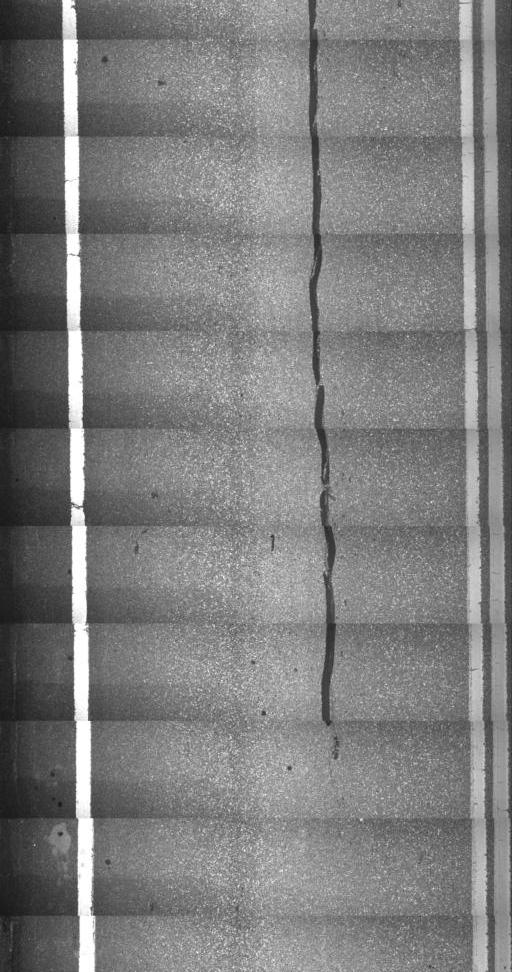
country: US
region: New Hampshire
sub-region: Grafton County
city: Orford
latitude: 43.9122
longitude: -72.2631
